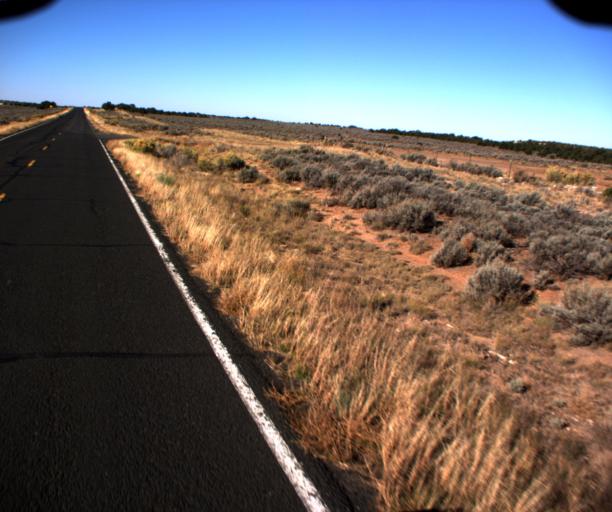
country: US
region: Arizona
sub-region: Navajo County
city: First Mesa
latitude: 35.7374
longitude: -110.0850
